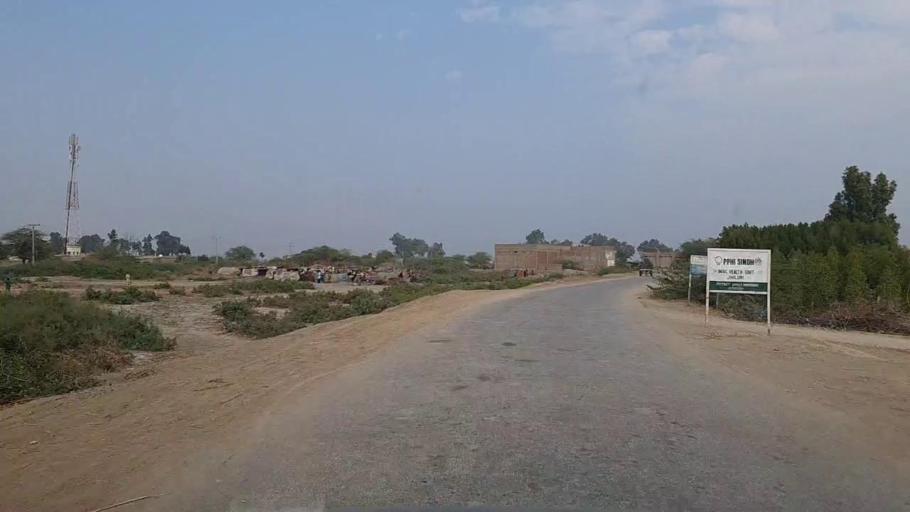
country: PK
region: Sindh
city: Mirwah Gorchani
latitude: 25.4255
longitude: 69.1522
